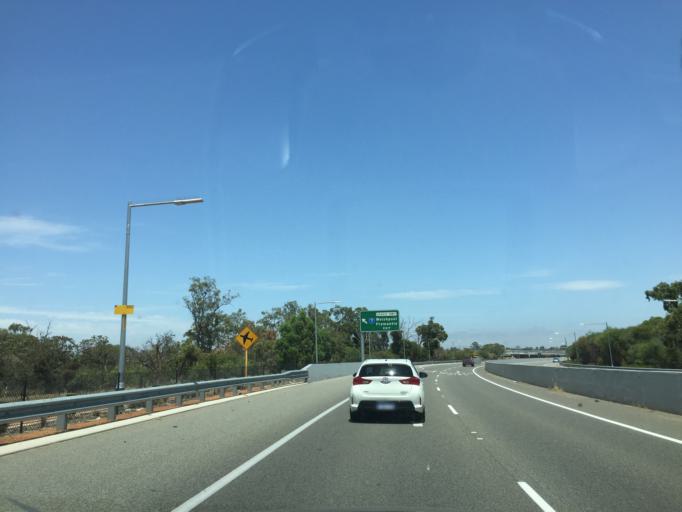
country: AU
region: Western Australia
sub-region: Belmont
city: Kewdale
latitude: -31.9634
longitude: 115.9635
